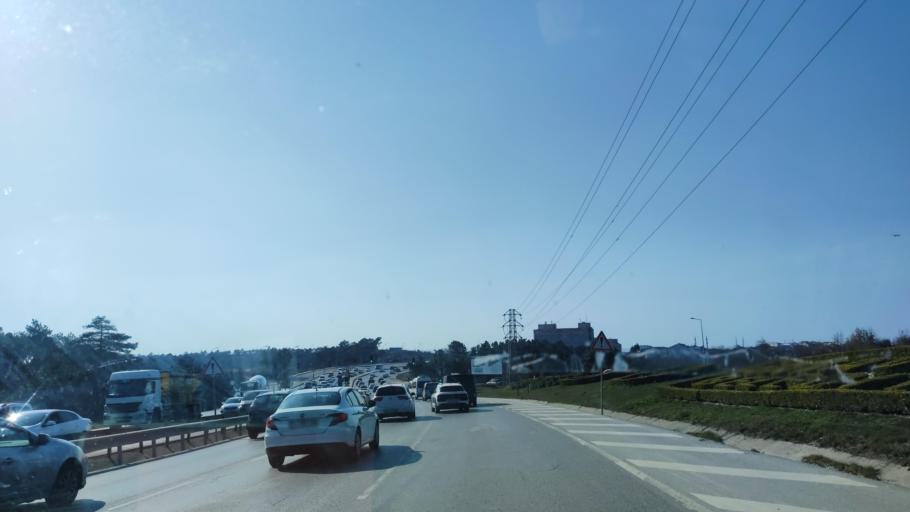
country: TR
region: Istanbul
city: Basaksehir
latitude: 41.1739
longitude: 28.7554
